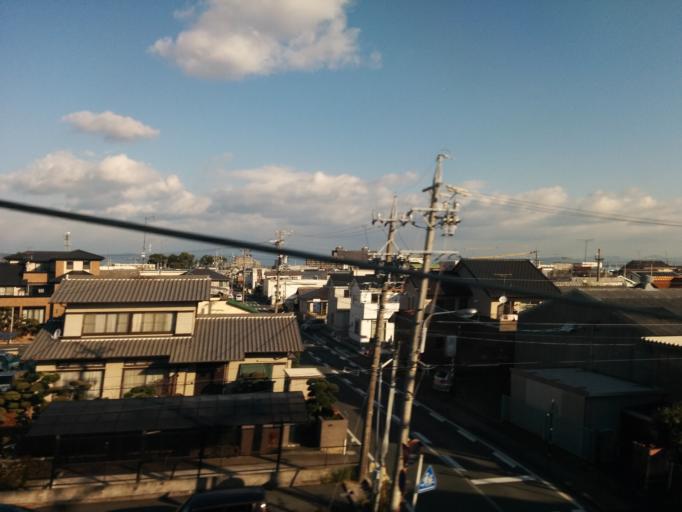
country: JP
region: Shizuoka
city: Hamamatsu
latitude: 34.7088
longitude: 137.7752
